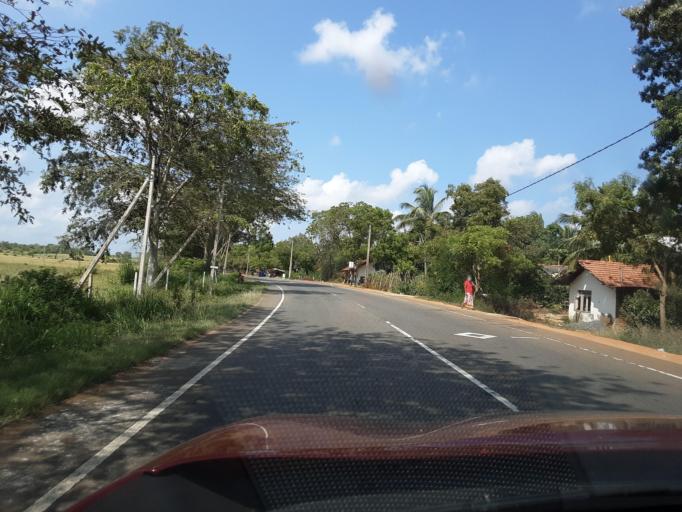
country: LK
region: Southern
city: Tangalla
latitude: 6.2206
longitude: 81.2167
